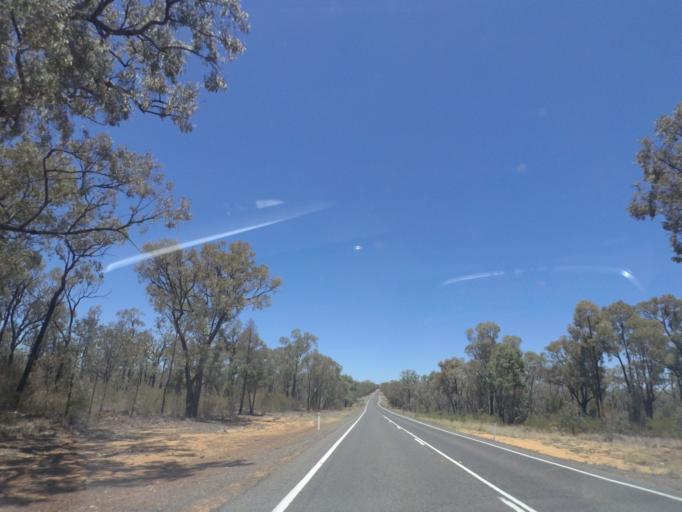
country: AU
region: New South Wales
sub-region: Narrabri
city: Narrabri
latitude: -30.7192
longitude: 149.5263
